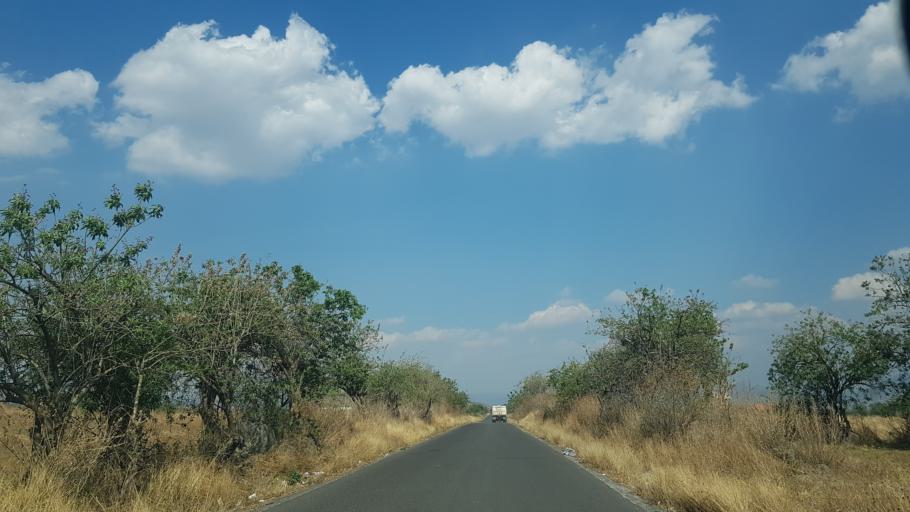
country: MX
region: Puebla
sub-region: Atlixco
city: Colonia Agricola de Ocotepec (Colonia San Jose)
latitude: 18.9236
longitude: -98.4995
